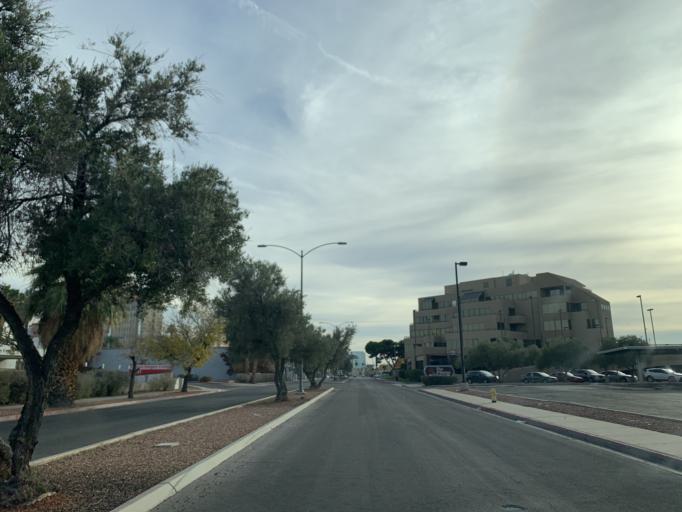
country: US
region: Nevada
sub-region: Clark County
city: Las Vegas
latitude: 36.1465
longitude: -115.1769
